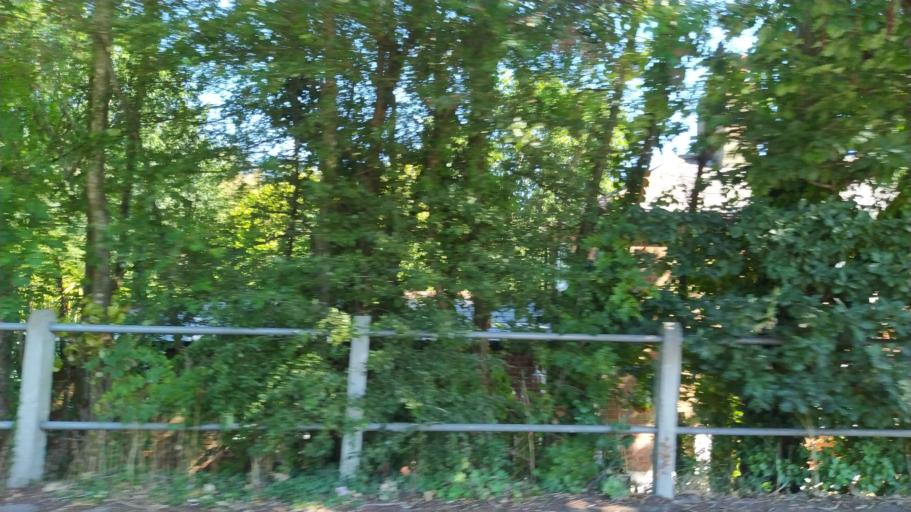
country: GB
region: England
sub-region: Hampshire
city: Totton
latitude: 50.9079
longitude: -1.4963
